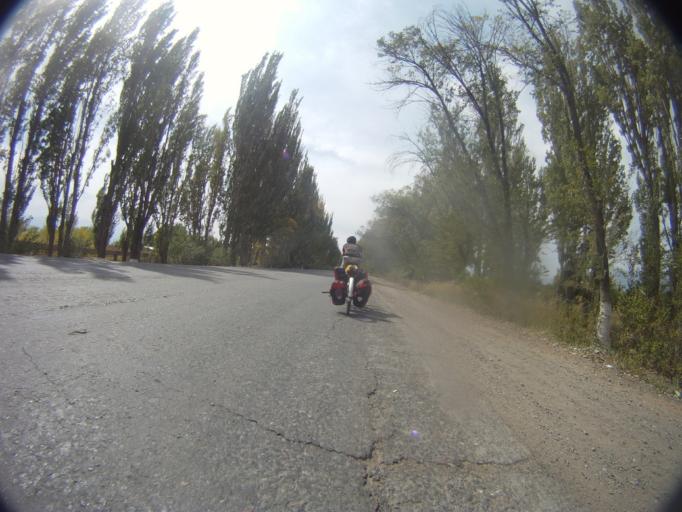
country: KG
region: Ysyk-Koel
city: Balykchy
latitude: 42.4803
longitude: 76.2618
